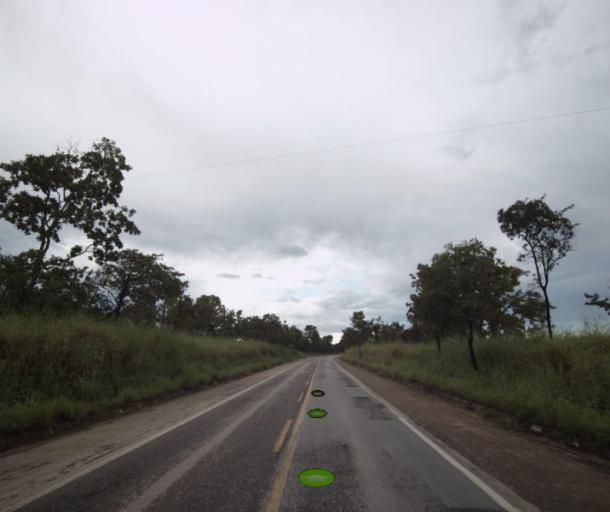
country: BR
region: Goias
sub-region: Porangatu
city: Porangatu
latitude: -13.6778
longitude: -49.0248
